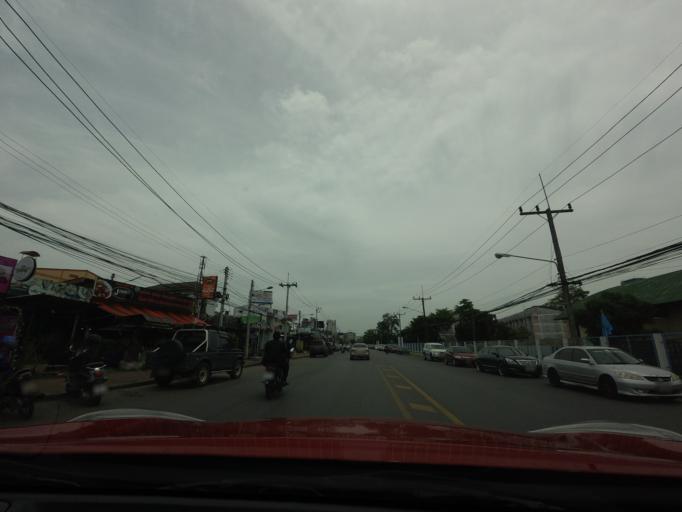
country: TH
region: Songkhla
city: Hat Yai
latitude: 7.0019
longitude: 100.4948
